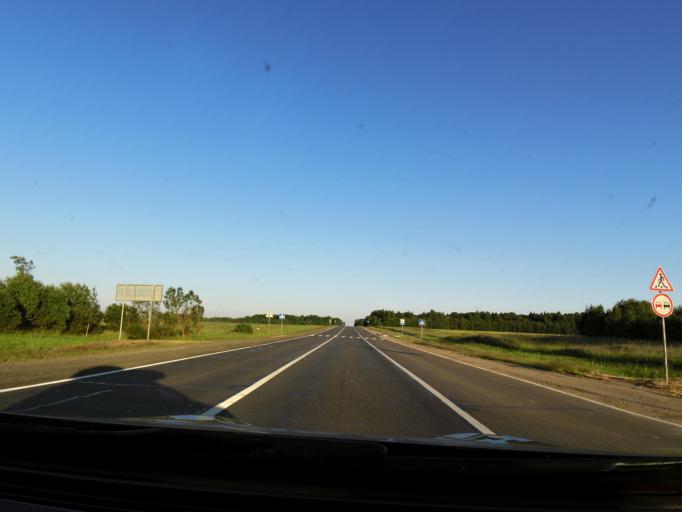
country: RU
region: Vologda
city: Gryazovets
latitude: 58.8198
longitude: 40.2283
